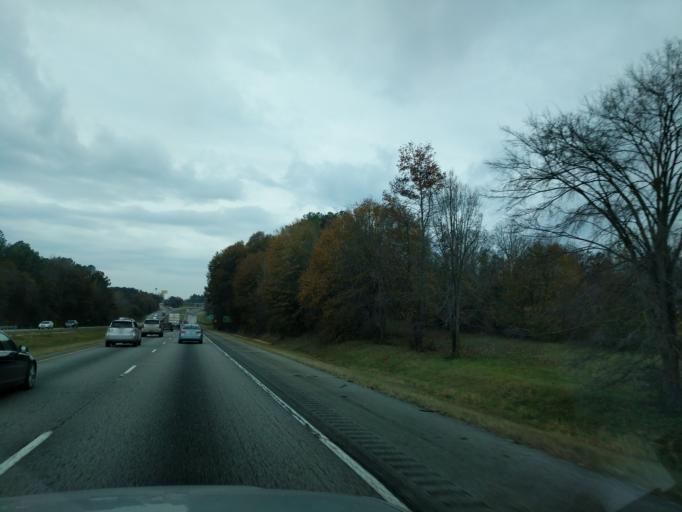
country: US
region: Georgia
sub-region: Franklin County
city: Carnesville
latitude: 34.3822
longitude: -83.2478
